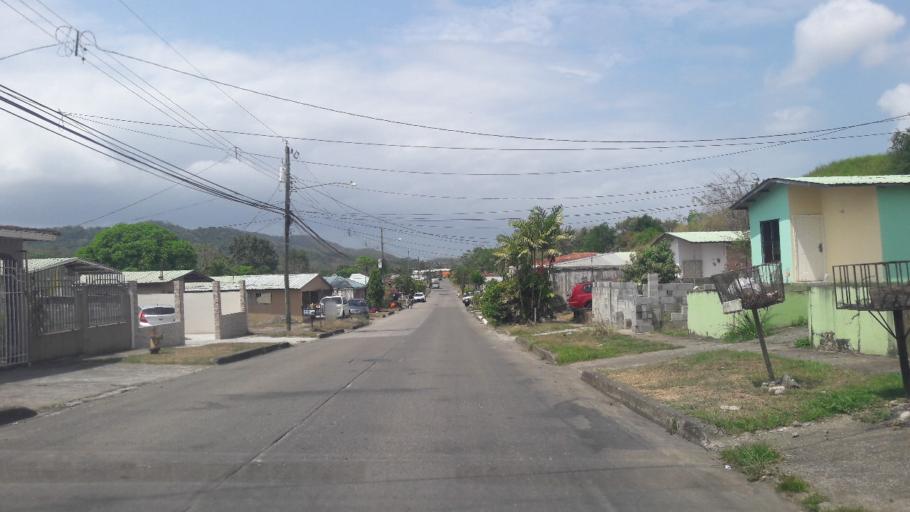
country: PA
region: Panama
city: Alcalde Diaz
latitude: 9.1387
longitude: -79.5511
